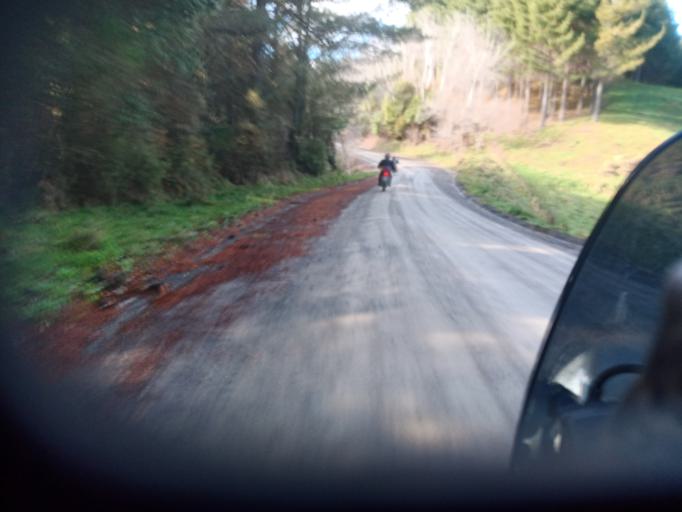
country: NZ
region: Gisborne
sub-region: Gisborne District
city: Gisborne
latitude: -38.0554
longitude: 178.1481
